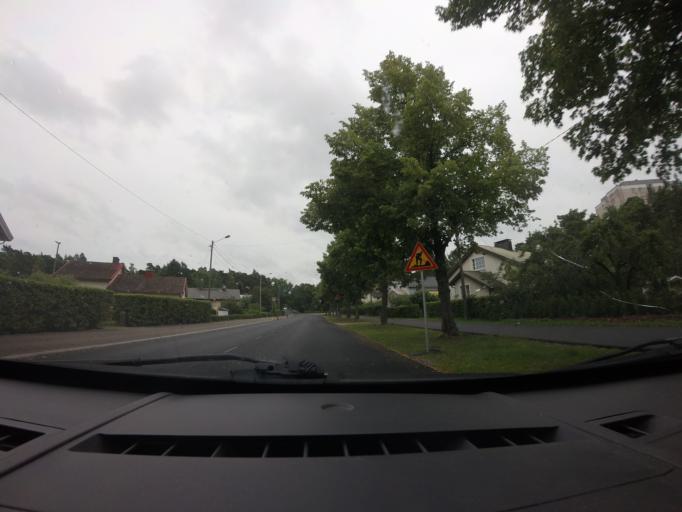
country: FI
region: Varsinais-Suomi
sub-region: Turku
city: Turku
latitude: 60.4339
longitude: 22.2762
